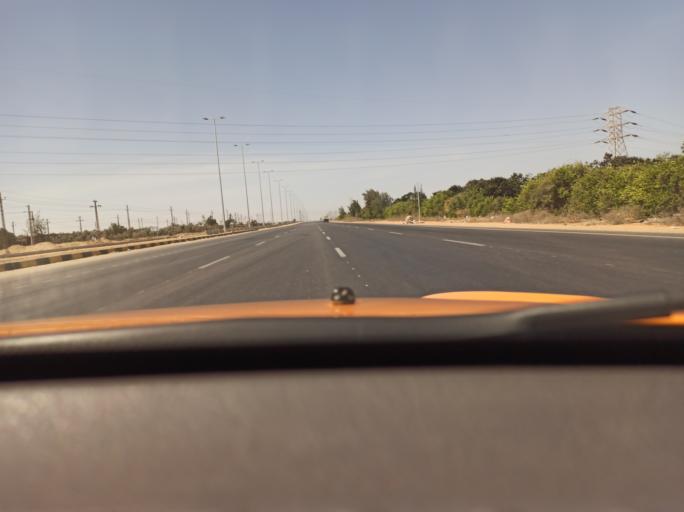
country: EG
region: Al Isma'iliyah
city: Ismailia
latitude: 30.5129
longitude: 32.1391
